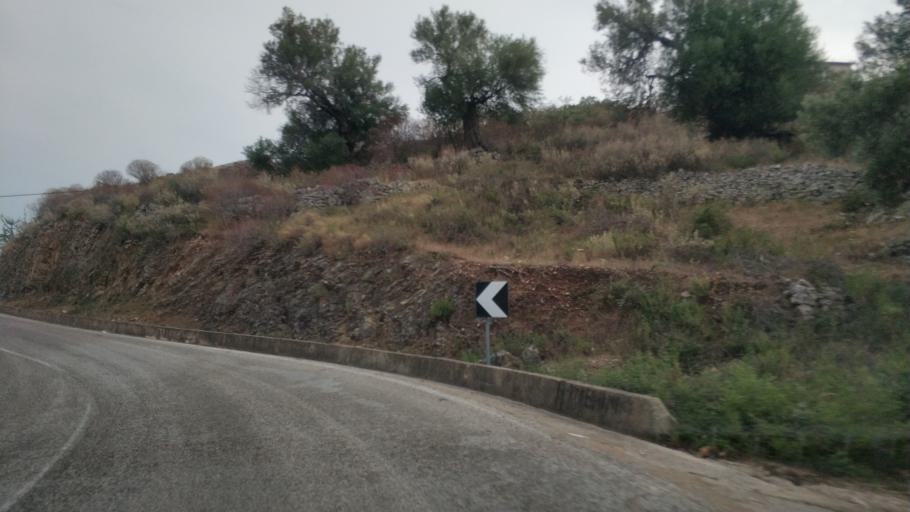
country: AL
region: Vlore
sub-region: Rrethi i Vlores
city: Himare
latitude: 40.0507
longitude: 19.8111
